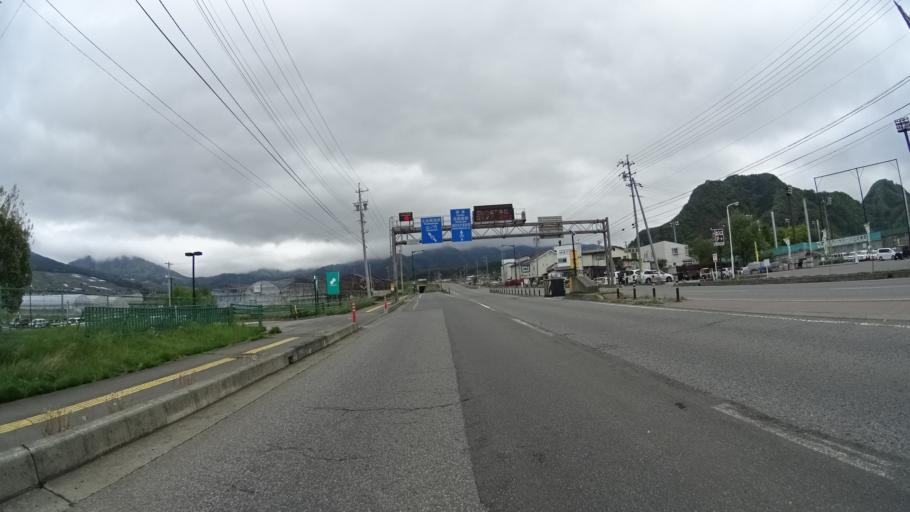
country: JP
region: Nagano
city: Nakano
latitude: 36.7587
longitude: 138.3804
